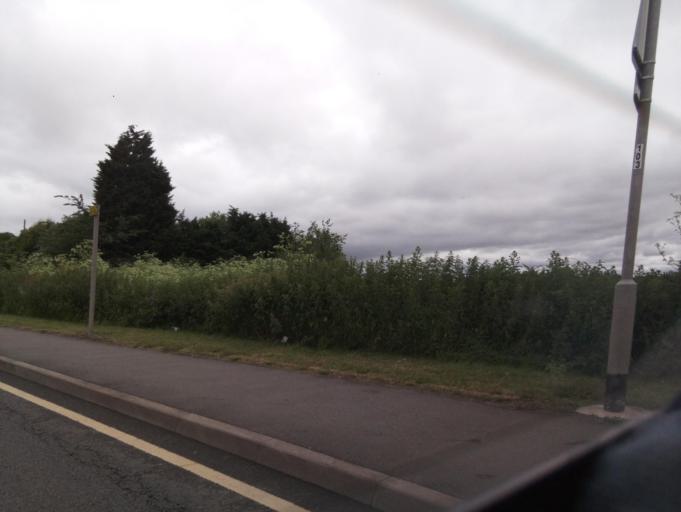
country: GB
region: England
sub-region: Staffordshire
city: Burton upon Trent
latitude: 52.8339
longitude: -1.6538
